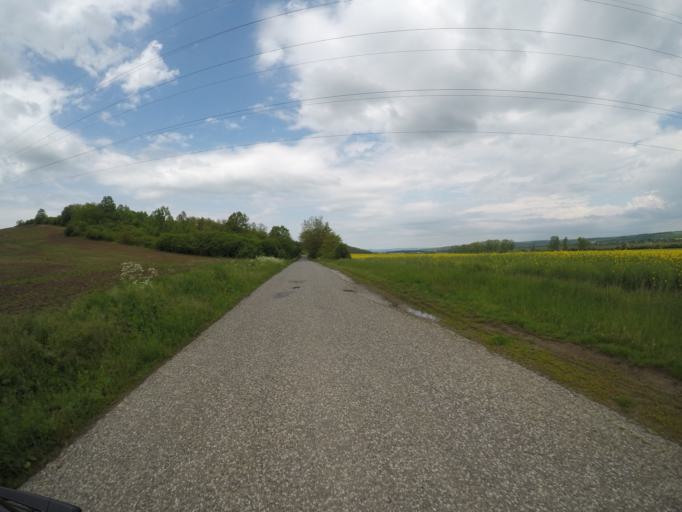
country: SK
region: Banskobystricky
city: Dudince
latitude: 48.0981
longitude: 18.8705
